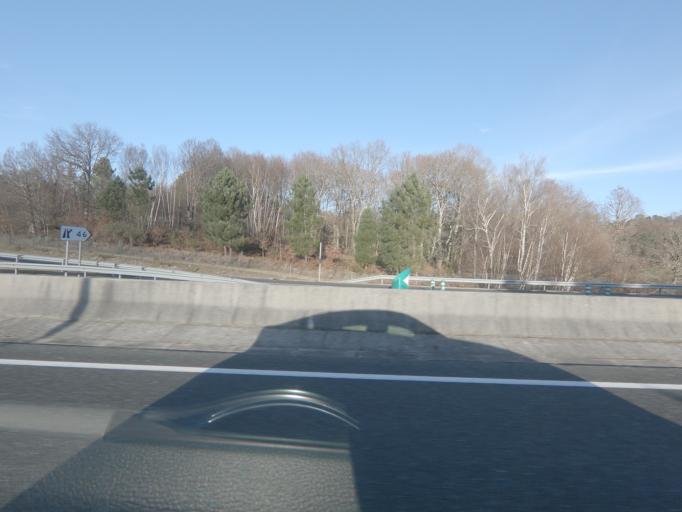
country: ES
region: Galicia
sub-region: Provincia de Pontevedra
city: Lalin
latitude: 42.6358
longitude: -8.1306
